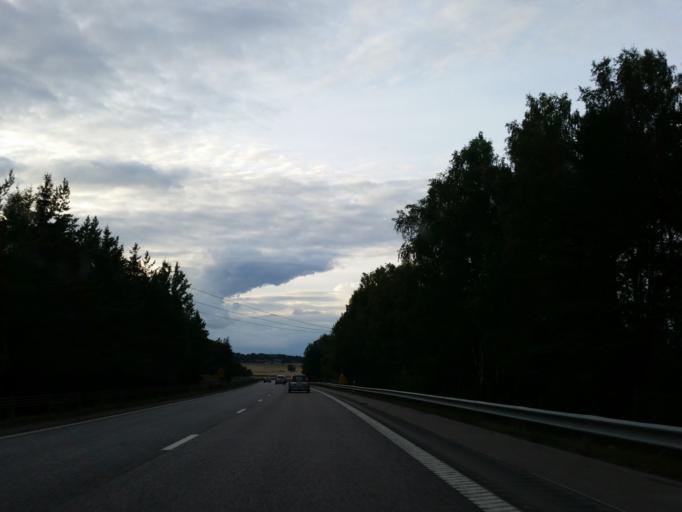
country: SE
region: Uppsala
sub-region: Uppsala Kommun
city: Alsike
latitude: 59.8013
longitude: 17.7679
